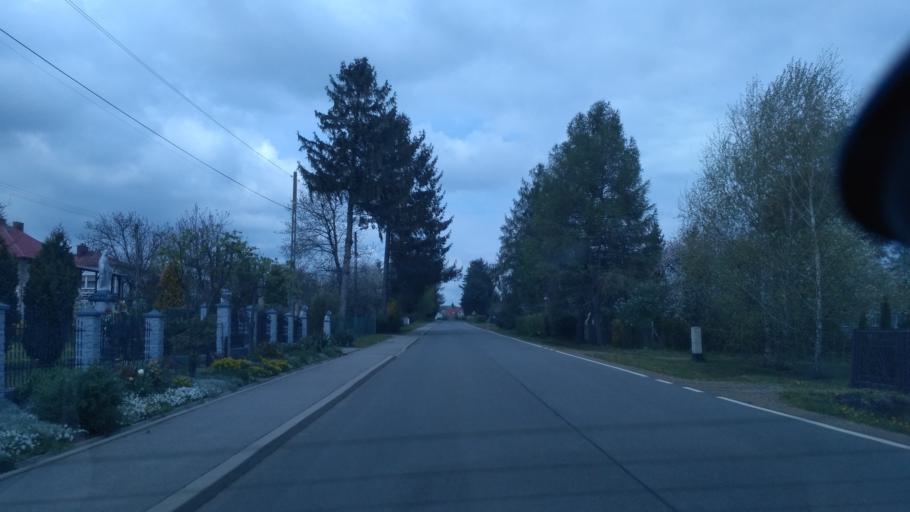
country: PL
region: Subcarpathian Voivodeship
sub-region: Powiat brzozowski
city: Jasionow
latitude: 49.6483
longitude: 21.9771
